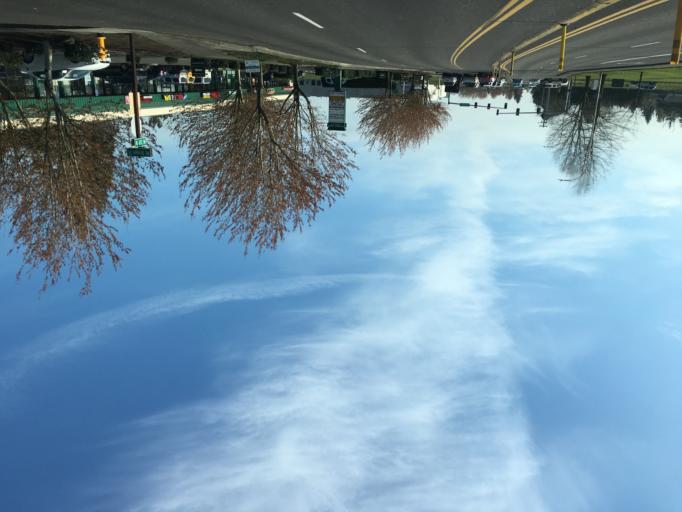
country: US
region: Oregon
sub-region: Multnomah County
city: Wood Village
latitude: 45.5291
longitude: -122.4131
